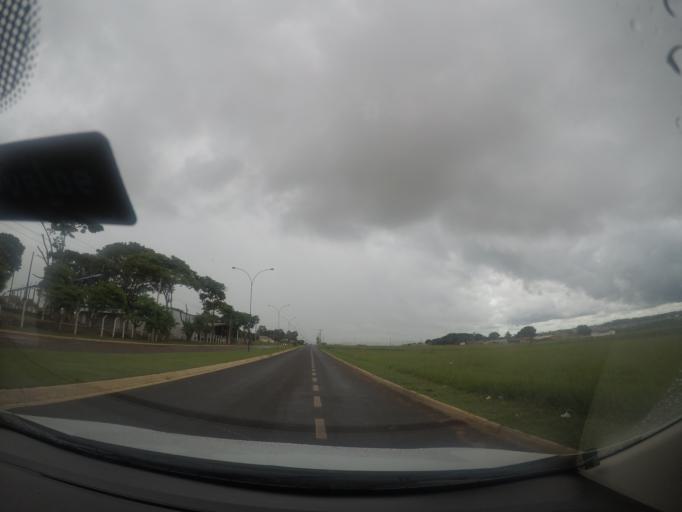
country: BR
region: Goias
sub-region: Trindade
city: Trindade
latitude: -16.6366
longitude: -49.4133
